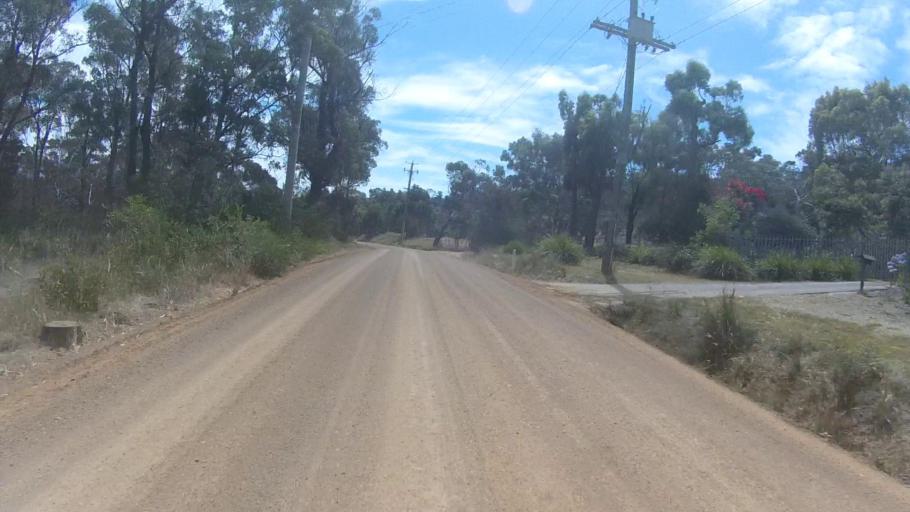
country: AU
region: Tasmania
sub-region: Kingborough
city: Blackmans Bay
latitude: -43.0424
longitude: 147.3062
